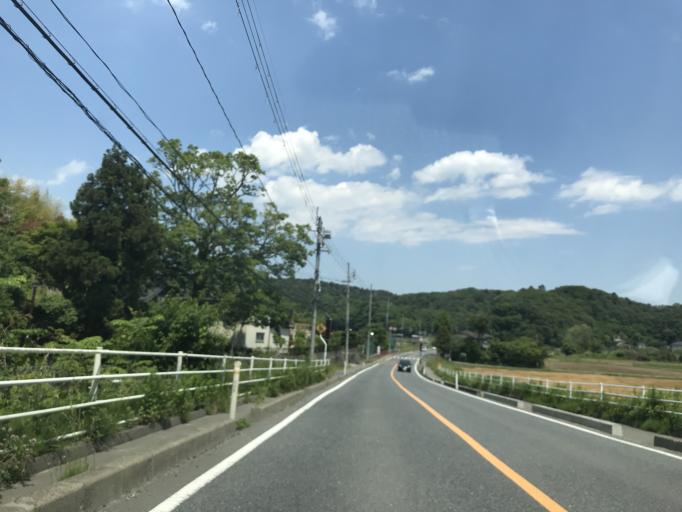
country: JP
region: Miyagi
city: Matsushima
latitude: 38.3893
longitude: 141.0997
